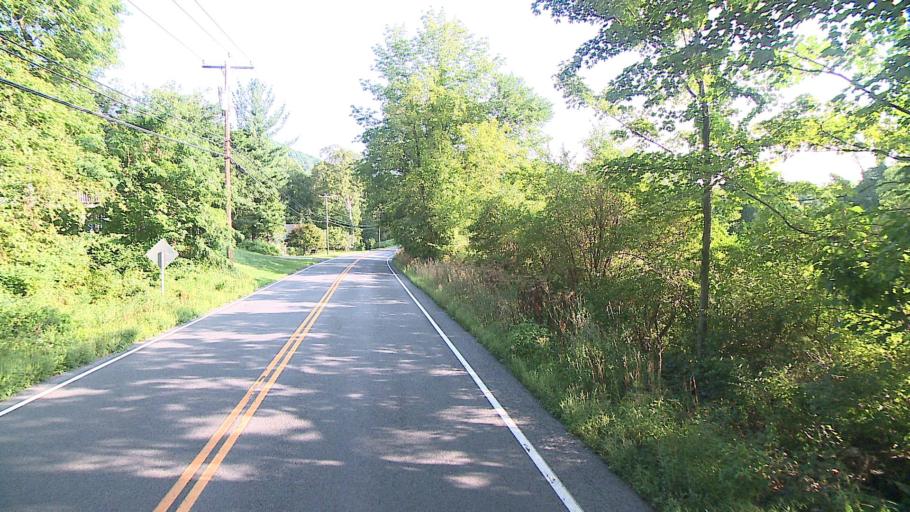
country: US
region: Connecticut
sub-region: Litchfield County
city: Kent
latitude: 41.7358
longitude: -73.4691
